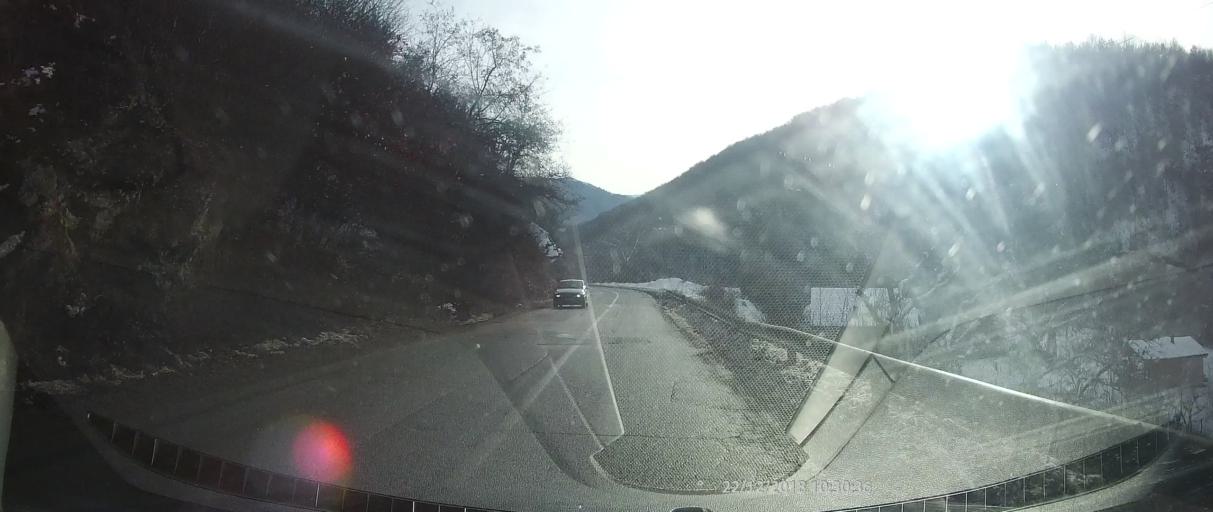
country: MK
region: Kriva Palanka
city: Kriva Palanka
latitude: 42.2255
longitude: 22.4130
